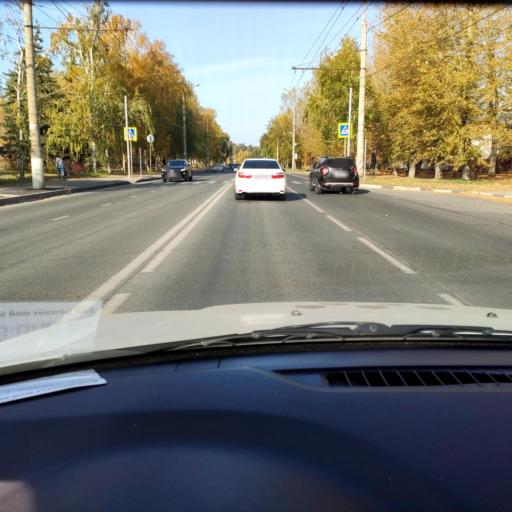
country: RU
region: Samara
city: Tol'yatti
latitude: 53.5024
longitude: 49.3903
